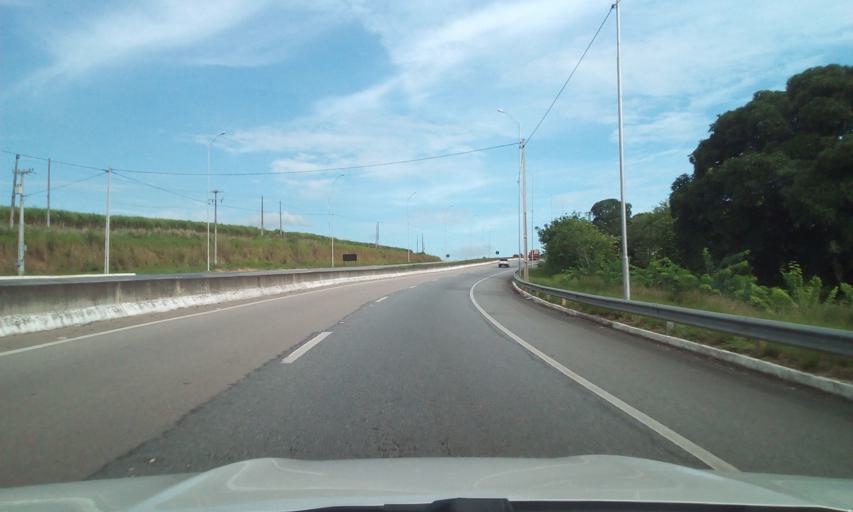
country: BR
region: Paraiba
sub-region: Santa Rita
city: Santa Rita
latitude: -7.0860
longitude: -34.9693
